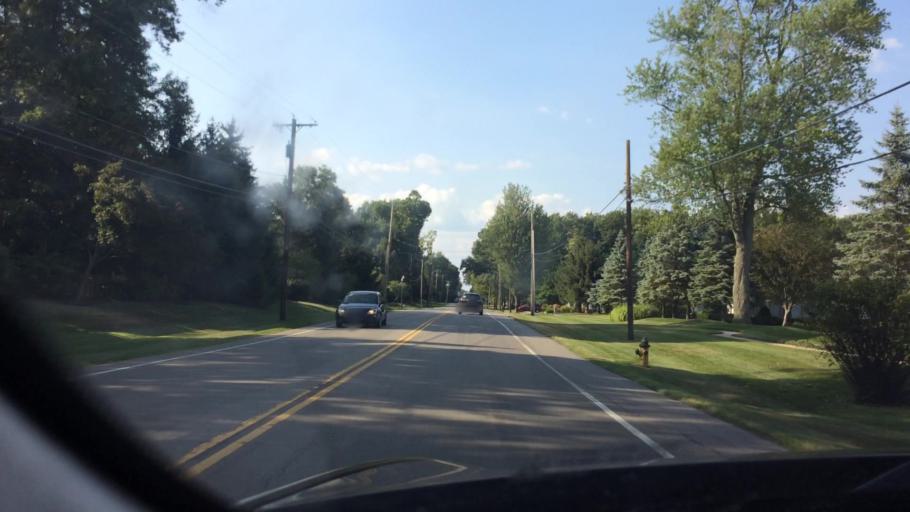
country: US
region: Ohio
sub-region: Lucas County
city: Holland
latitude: 41.6612
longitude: -83.7222
